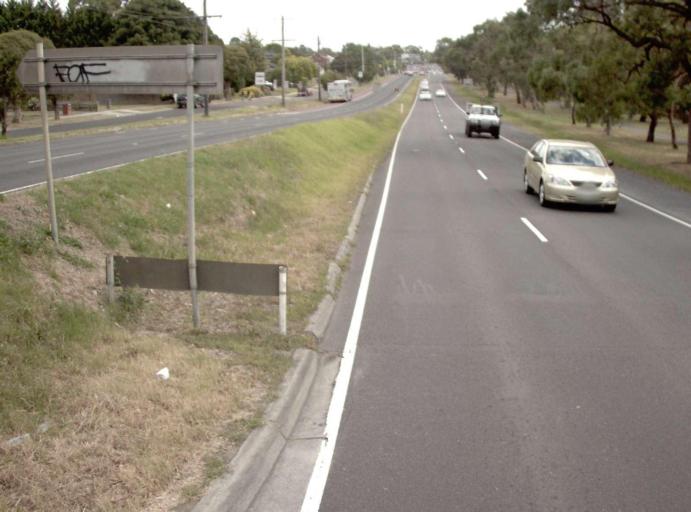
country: AU
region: Victoria
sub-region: Knox
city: Wantirna
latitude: -37.8617
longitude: 145.2389
